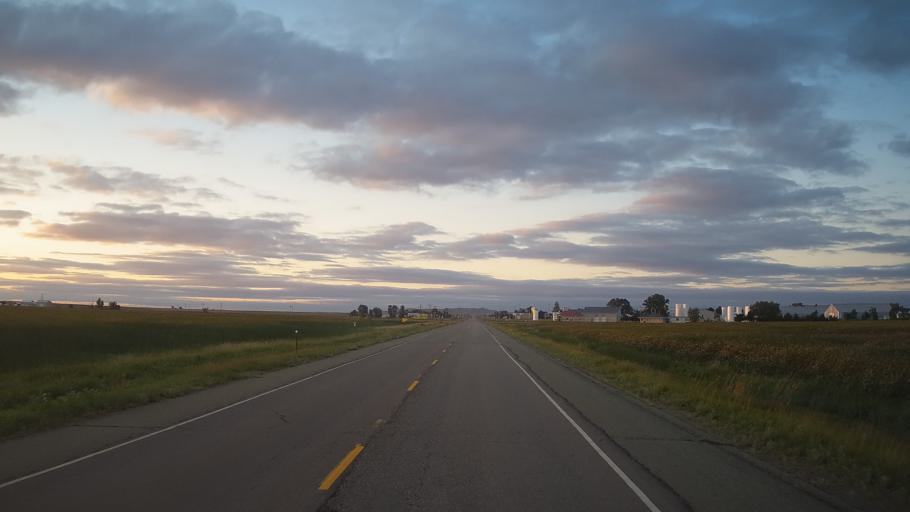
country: US
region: South Dakota
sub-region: Lyman County
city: Kennebec
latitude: 43.8718
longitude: -99.6060
